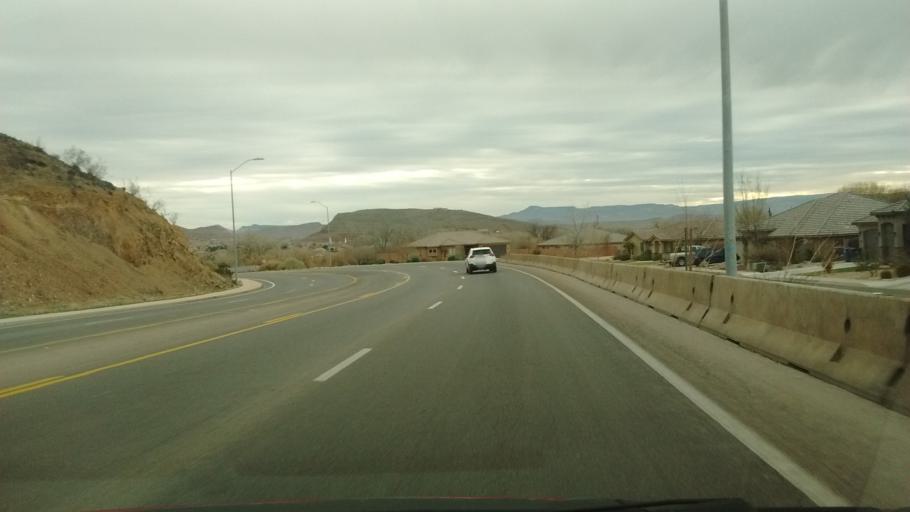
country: US
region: Utah
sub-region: Washington County
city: Washington
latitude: 37.1198
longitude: -113.5047
